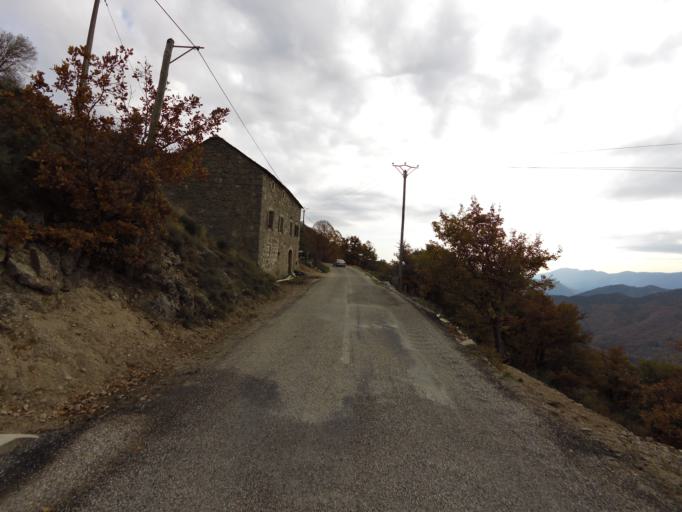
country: FR
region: Rhone-Alpes
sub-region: Departement de l'Ardeche
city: Les Vans
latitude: 44.5133
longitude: 4.0350
